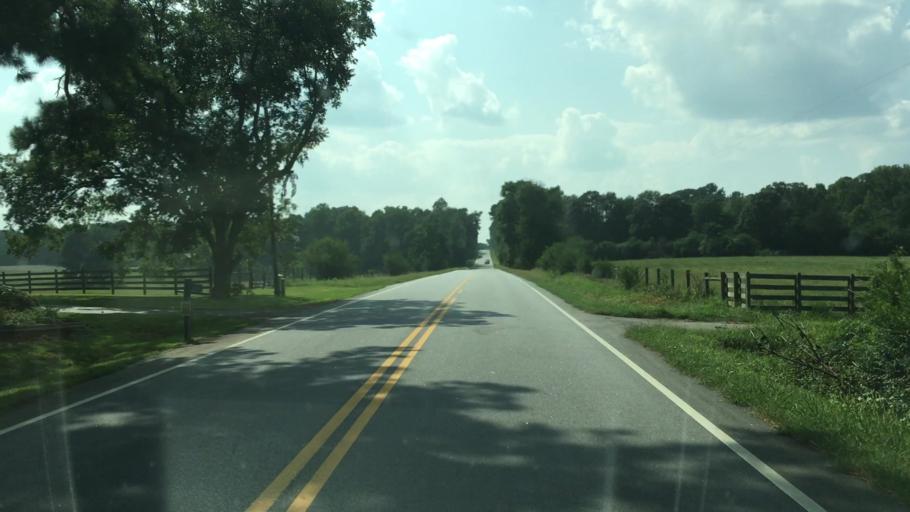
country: US
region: Georgia
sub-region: Jasper County
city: Monticello
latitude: 33.3546
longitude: -83.7345
